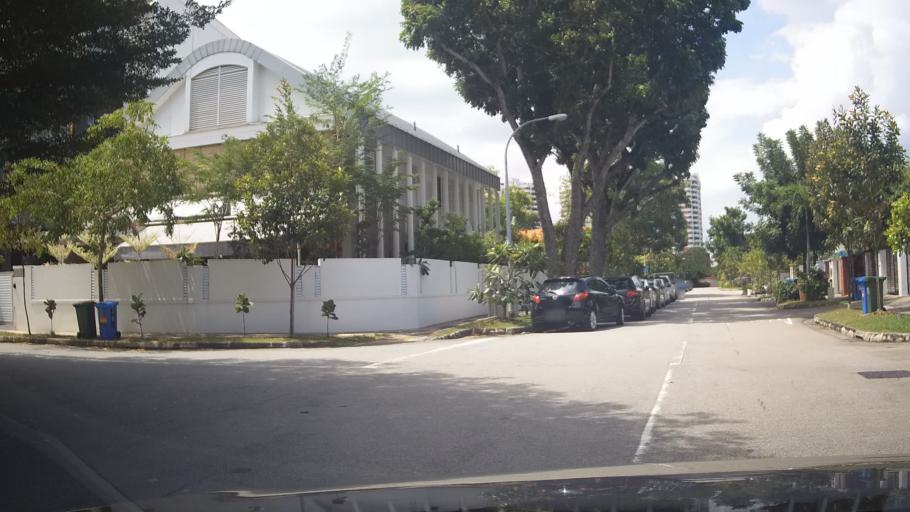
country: SG
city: Singapore
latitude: 1.3110
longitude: 103.9229
